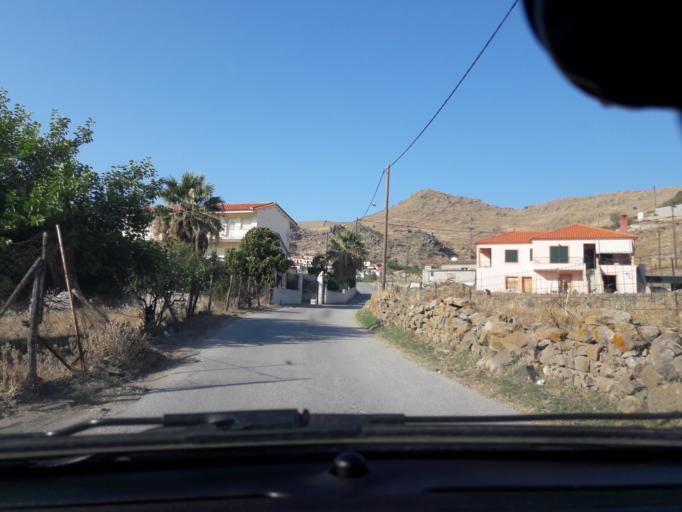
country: GR
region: North Aegean
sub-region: Nomos Lesvou
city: Myrina
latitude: 39.8505
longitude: 25.0862
